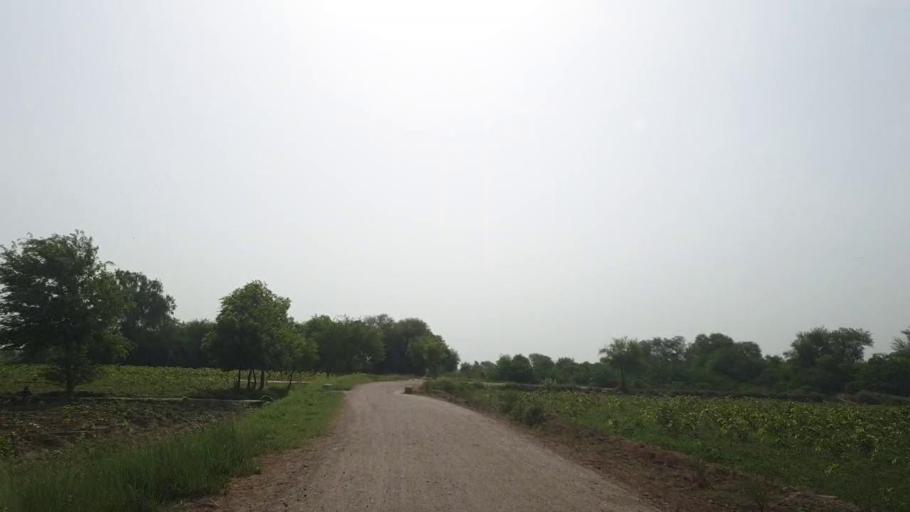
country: PK
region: Sindh
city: Nawabshah
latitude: 26.1153
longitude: 68.4328
